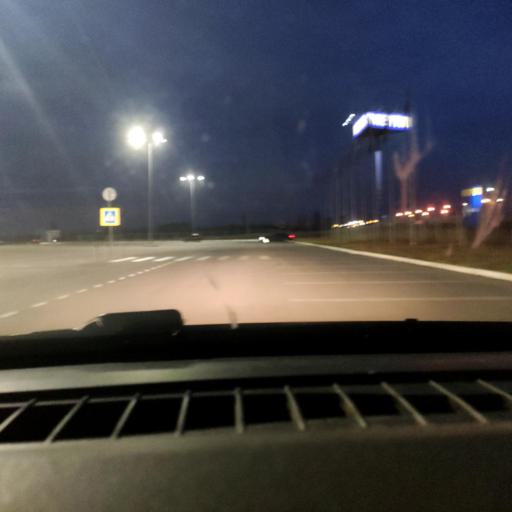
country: RU
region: Voronezj
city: Pridonskoy
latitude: 51.6524
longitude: 39.0616
